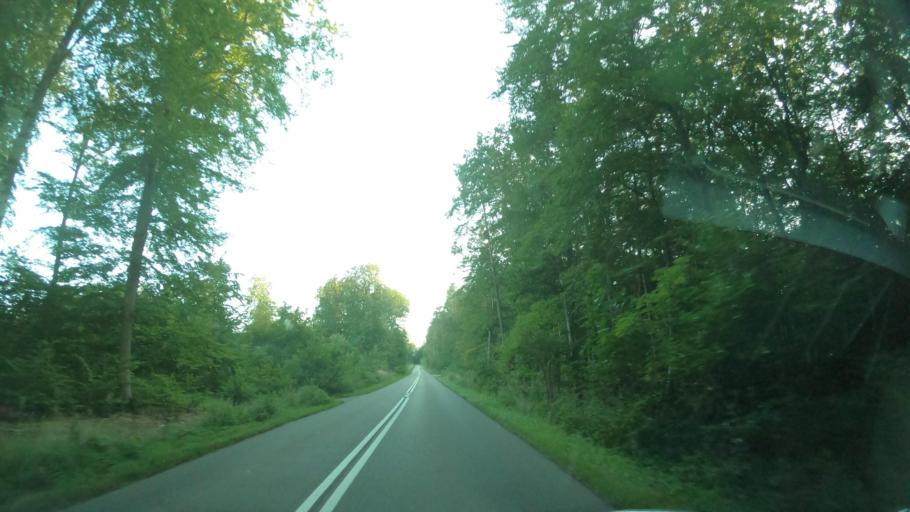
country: PL
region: West Pomeranian Voivodeship
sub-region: Powiat policki
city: Police
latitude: 53.5166
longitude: 14.5218
